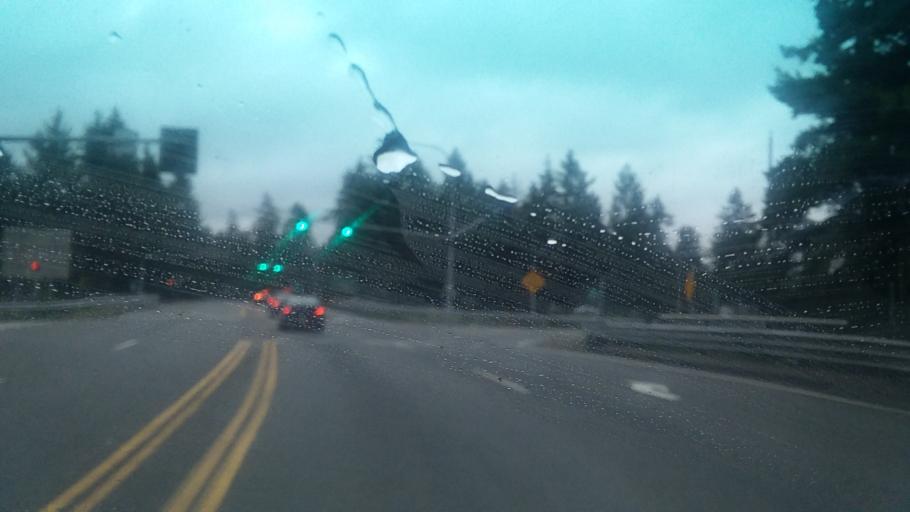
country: US
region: Washington
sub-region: Pierce County
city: McChord Air Force Base
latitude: 47.1376
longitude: -122.5260
